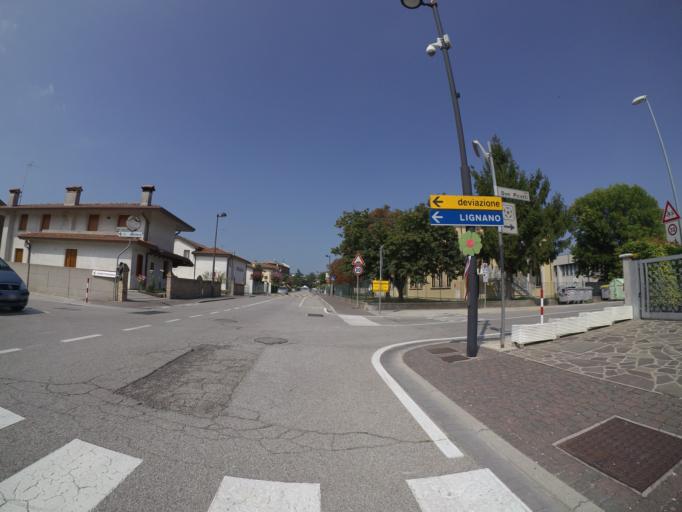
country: IT
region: Friuli Venezia Giulia
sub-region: Provincia di Udine
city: Pertegada
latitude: 45.7217
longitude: 13.0443
